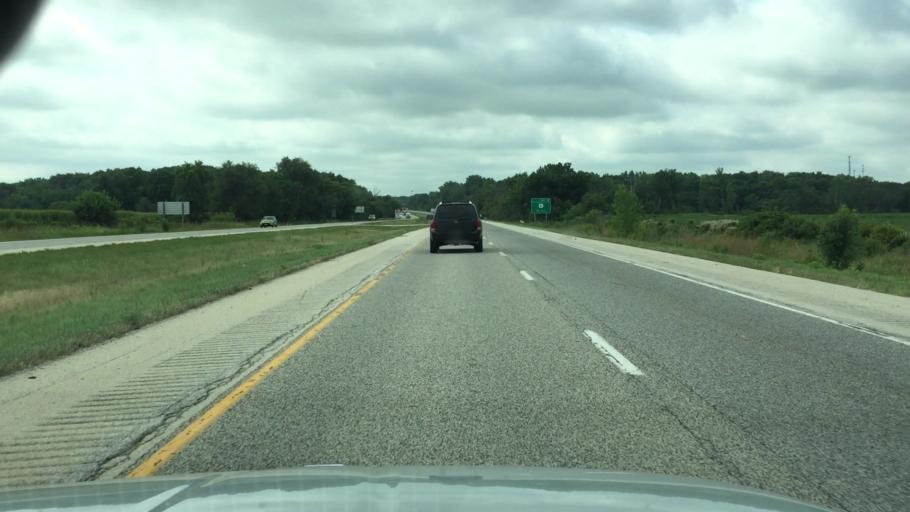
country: US
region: Illinois
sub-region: Henry County
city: Green Rock
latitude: 41.4683
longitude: -90.3389
